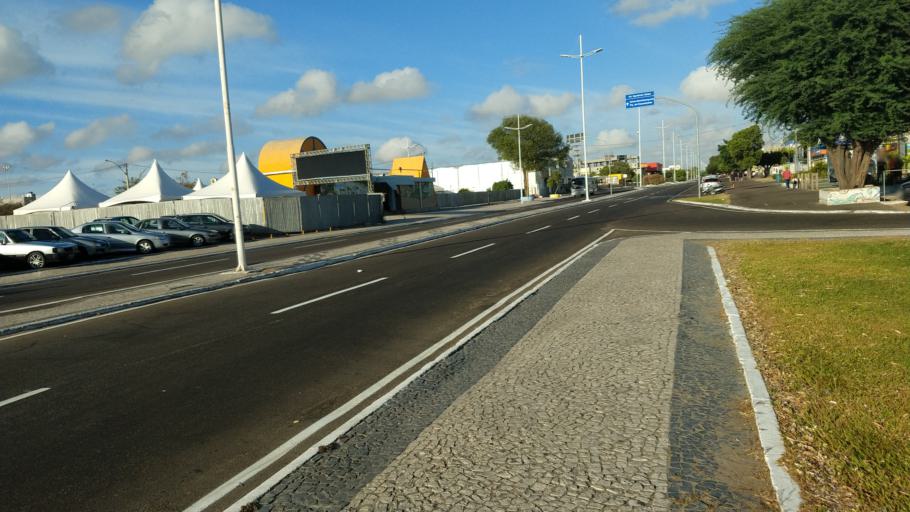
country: BR
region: Bahia
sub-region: Paulo Afonso
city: Paulo Afonso
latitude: -9.3982
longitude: -38.2191
